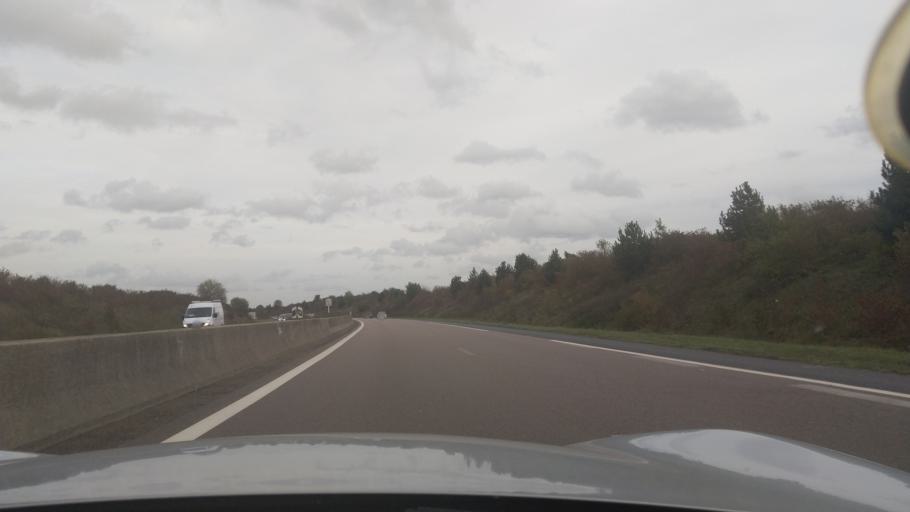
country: FR
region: Ile-de-France
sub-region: Departement du Val-d'Oise
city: Louvres
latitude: 49.0274
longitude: 2.5077
